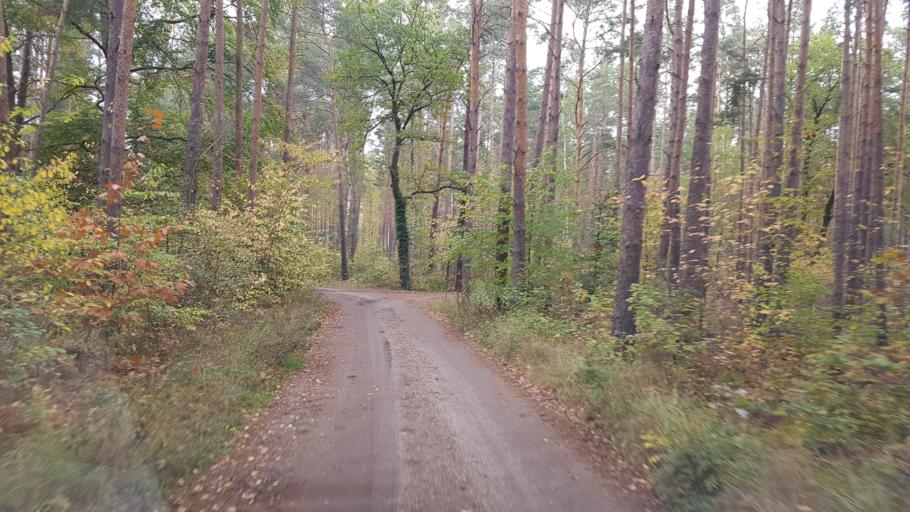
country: DE
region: Brandenburg
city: Schonborn
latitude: 51.6184
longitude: 13.5129
